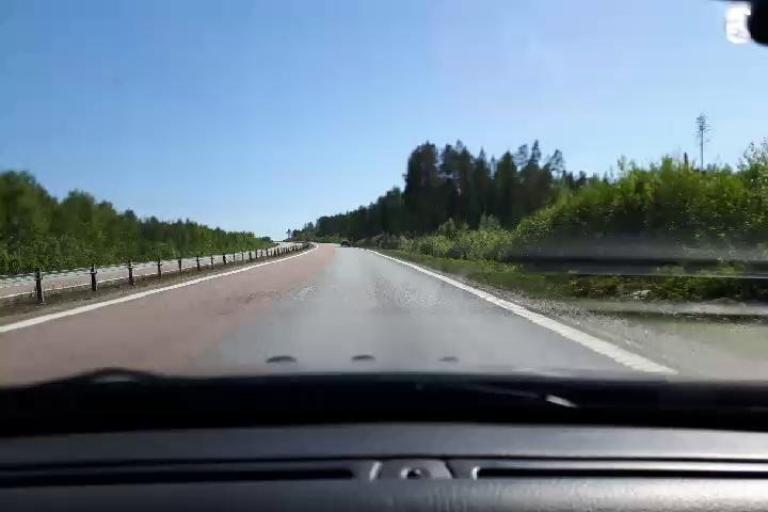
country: SE
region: Gaevleborg
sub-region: Soderhamns Kommun
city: Soderhamn
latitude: 61.3995
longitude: 16.9920
